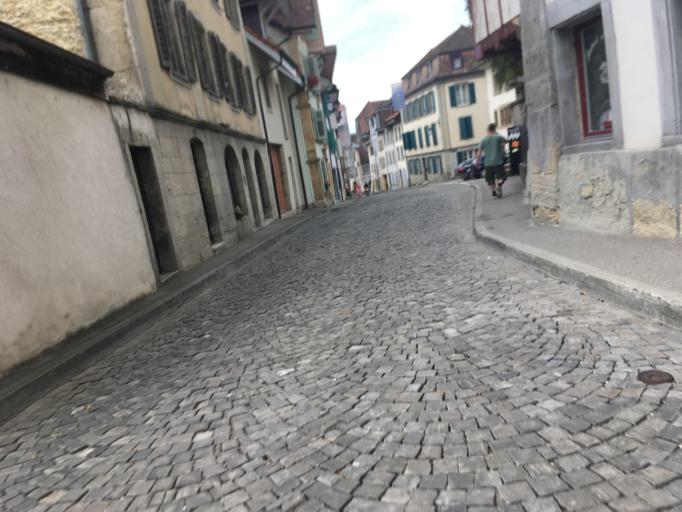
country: CH
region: Fribourg
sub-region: Broye District
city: Estavayer-le-Lac
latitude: 46.8496
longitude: 6.8491
